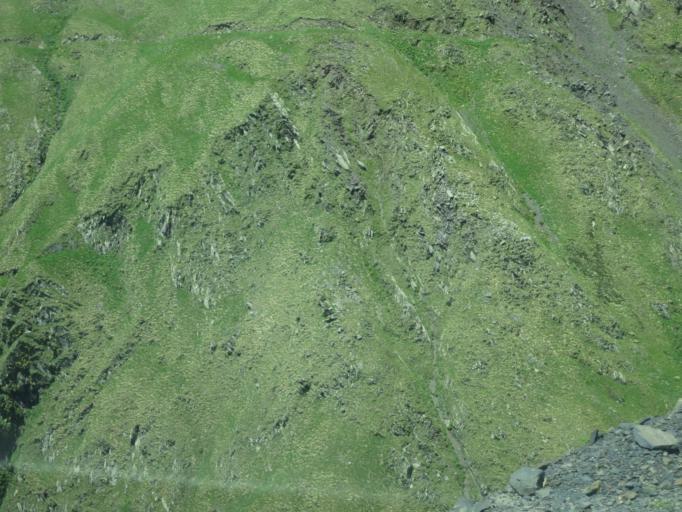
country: GE
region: Kakheti
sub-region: Telavi
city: Telavi
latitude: 42.2758
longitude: 45.4922
